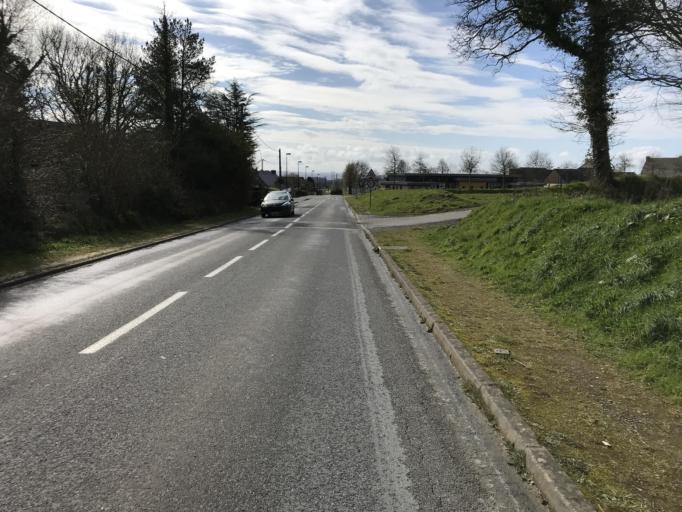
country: FR
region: Brittany
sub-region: Departement du Finistere
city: Dirinon
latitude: 48.3984
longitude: -4.2644
